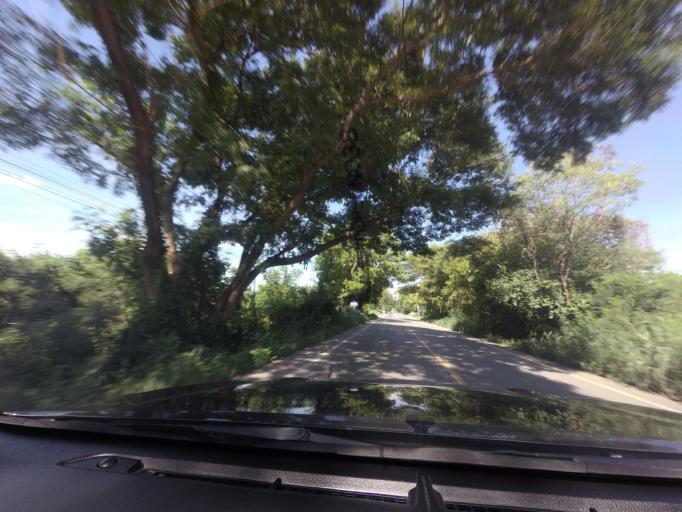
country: TH
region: Suphan Buri
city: Song Phi Nong
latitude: 14.1655
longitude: 99.9140
